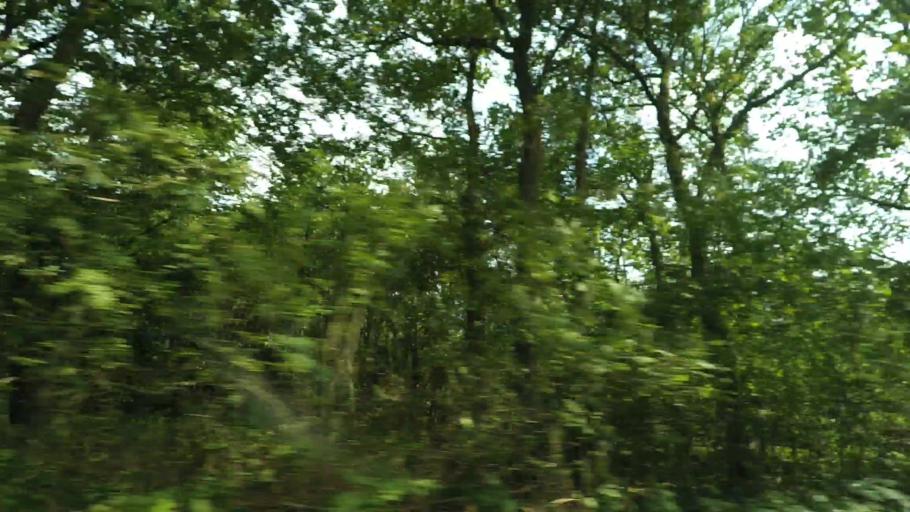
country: DK
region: Central Jutland
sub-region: Syddjurs Kommune
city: Ryomgard
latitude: 56.4594
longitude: 10.5375
